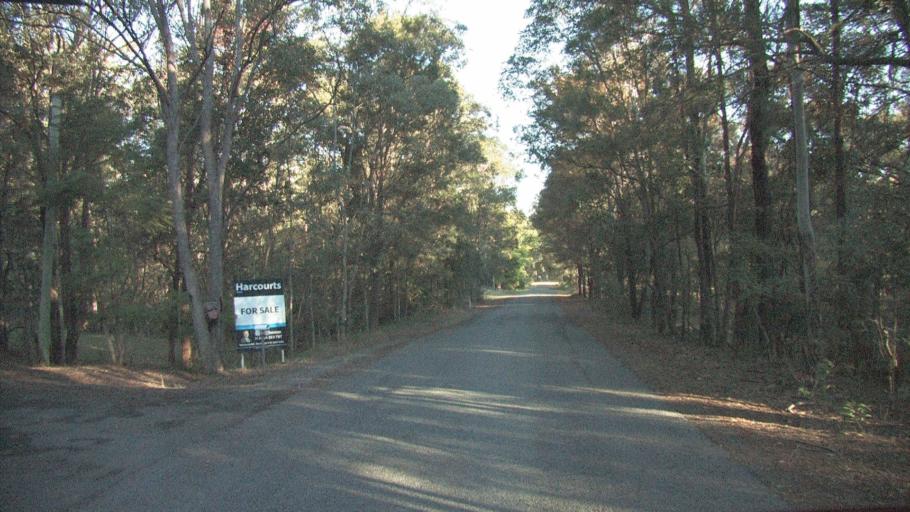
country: AU
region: Queensland
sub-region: Logan
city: Windaroo
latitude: -27.7441
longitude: 153.1485
